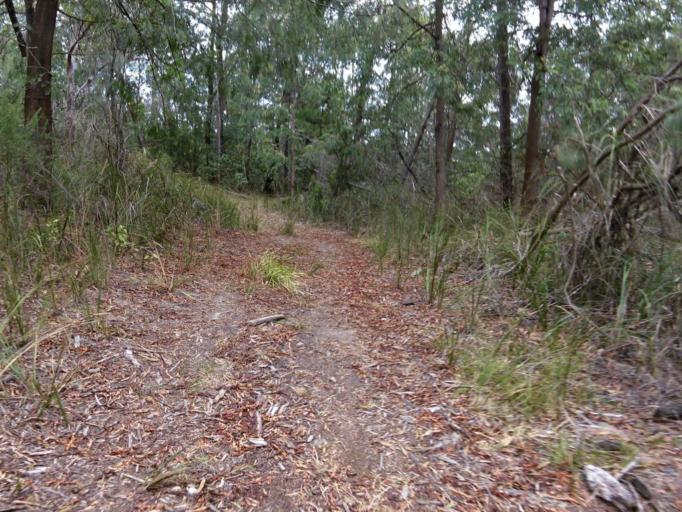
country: AU
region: Victoria
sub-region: Frankston
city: Frankston South
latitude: -38.1736
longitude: 145.1324
